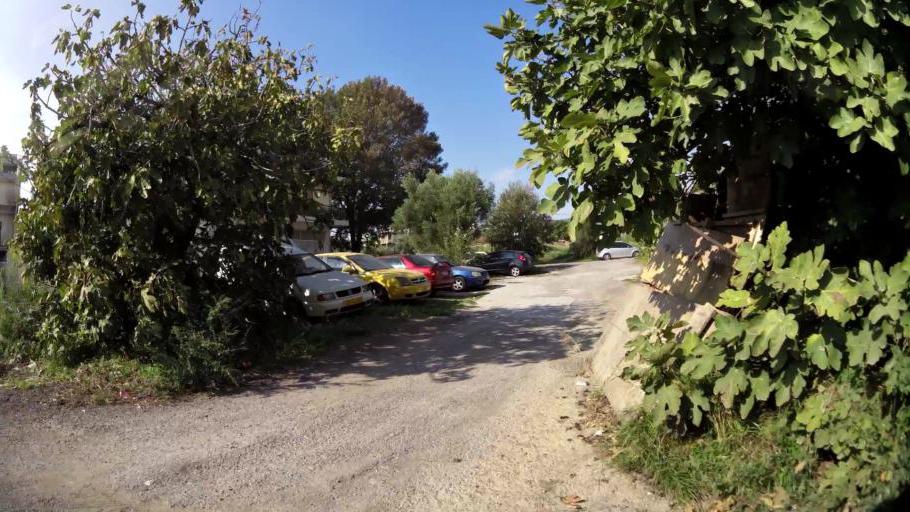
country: GR
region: Attica
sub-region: Nomarchia Athinas
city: Kamateron
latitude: 38.0551
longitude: 23.7068
